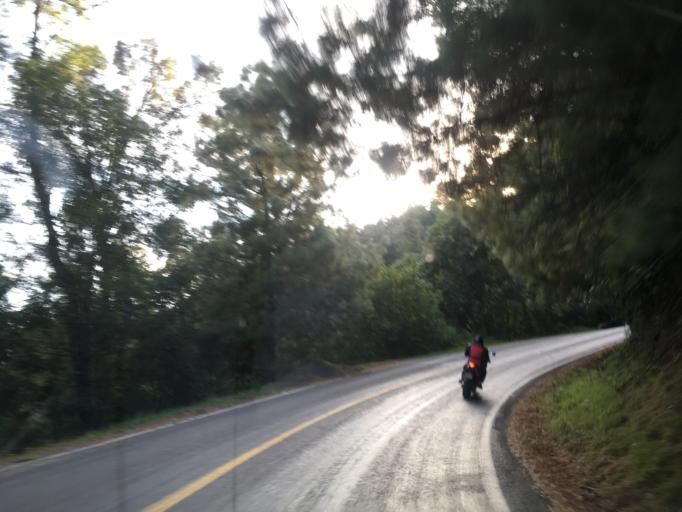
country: MX
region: Michoacan
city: Tzitzio
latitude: 19.6825
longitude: -100.8892
